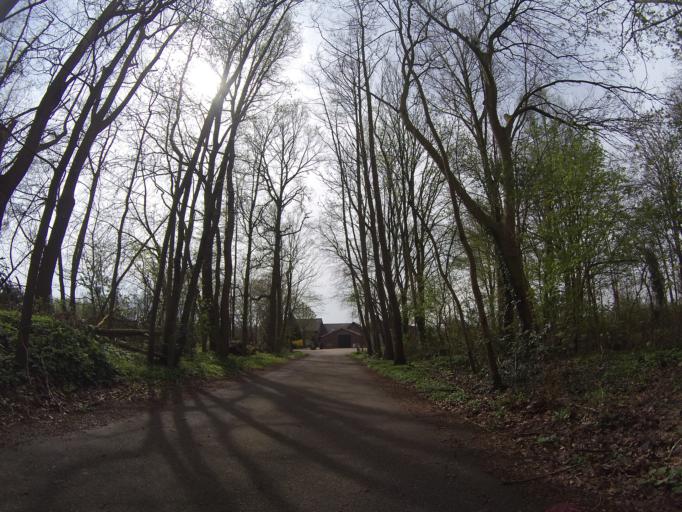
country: NL
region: Gelderland
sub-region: Gemeente Barneveld
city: Barneveld
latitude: 52.1562
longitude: 5.5934
